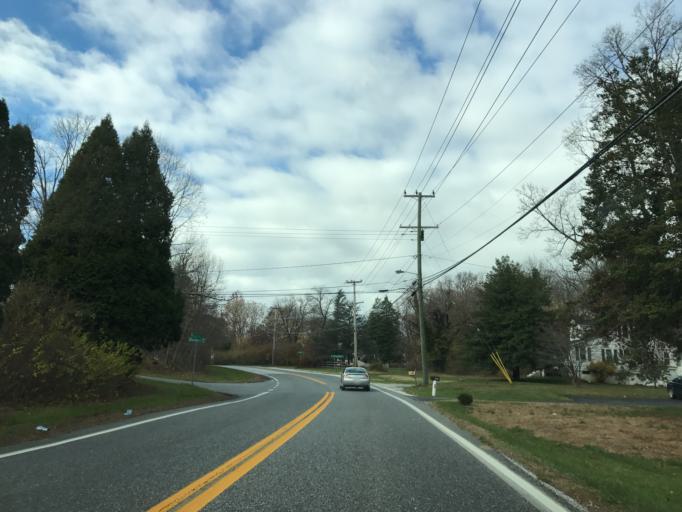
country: US
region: Maryland
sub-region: Baltimore County
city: Hunt Valley
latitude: 39.5136
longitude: -76.5461
